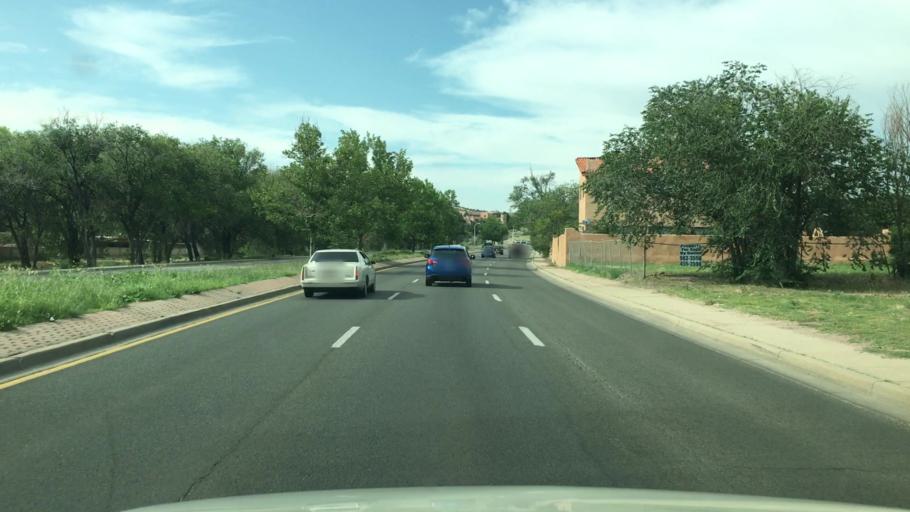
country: US
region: New Mexico
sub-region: Santa Fe County
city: Santa Fe
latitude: 35.6923
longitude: -105.9542
